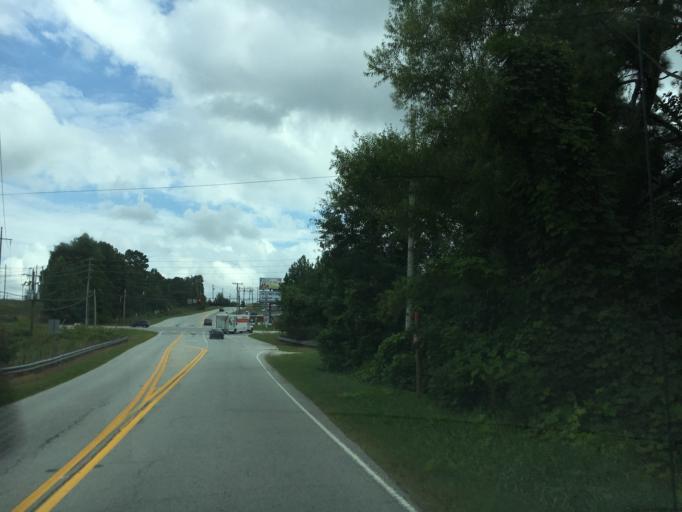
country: US
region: Georgia
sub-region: Rockdale County
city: Lakeview Estates
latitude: 33.6877
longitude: -84.0334
